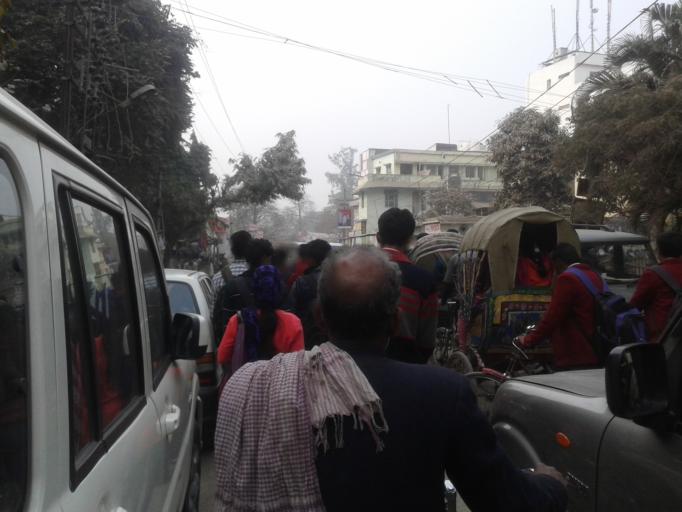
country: IN
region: Bihar
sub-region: Muzaffarpur
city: Muzaffarpur
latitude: 26.1148
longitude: 85.3957
